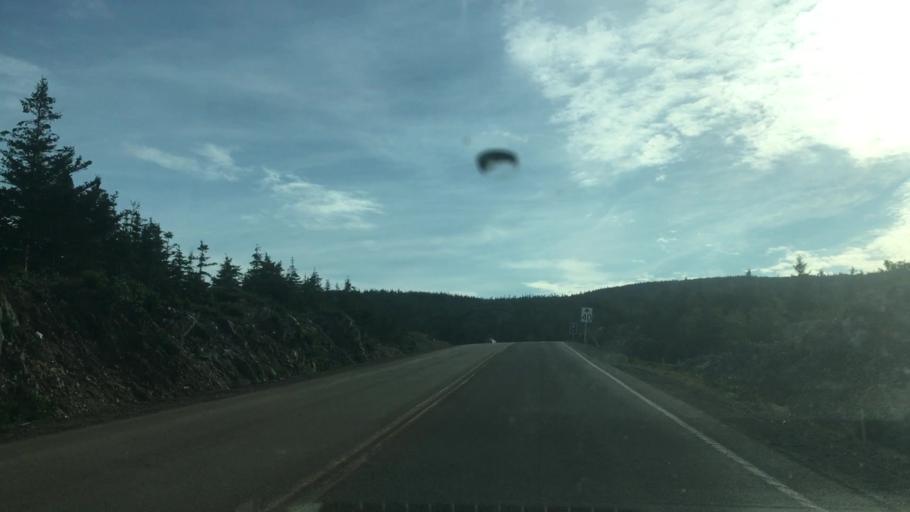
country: CA
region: Nova Scotia
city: Sydney Mines
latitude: 46.8190
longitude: -60.8324
